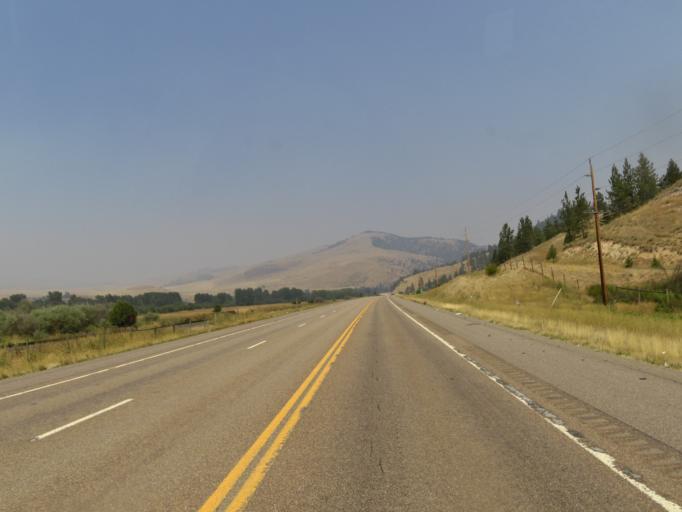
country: US
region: Montana
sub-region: Missoula County
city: Frenchtown
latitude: 47.2355
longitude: -114.1573
